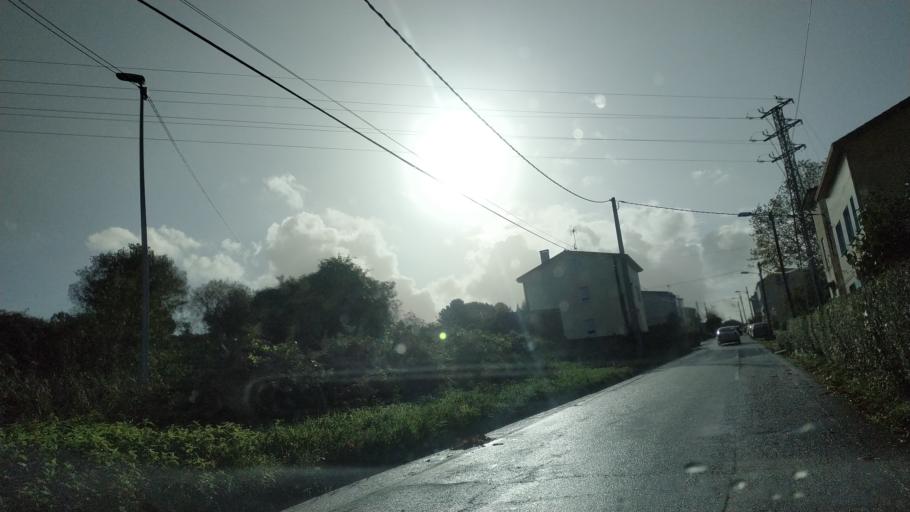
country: ES
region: Galicia
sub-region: Provincia da Coruna
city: A Coruna
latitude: 43.3334
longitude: -8.4053
